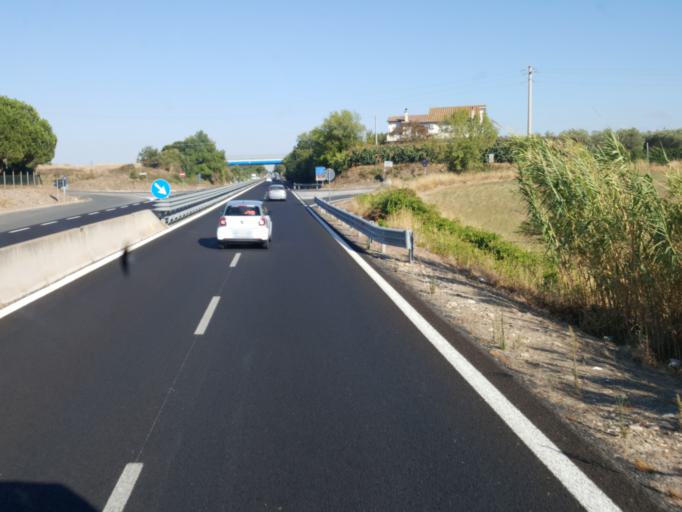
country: IT
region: Latium
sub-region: Provincia di Viterbo
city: Pescia Romana
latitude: 42.3959
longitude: 11.5220
